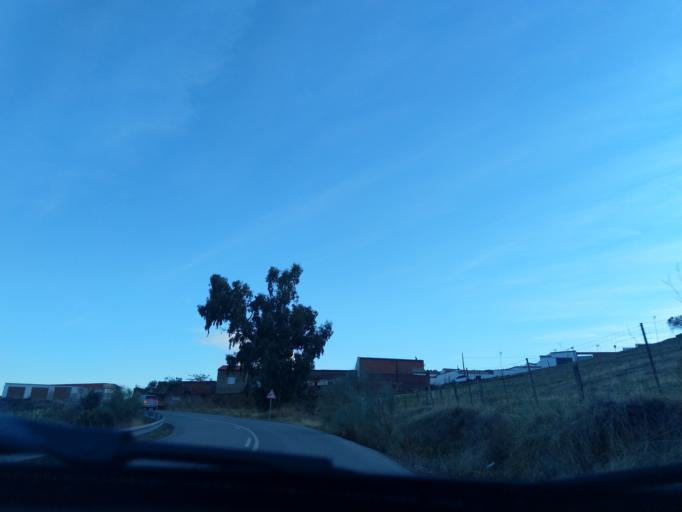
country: ES
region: Extremadura
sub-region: Provincia de Badajoz
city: Reina
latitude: 38.1564
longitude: -5.8974
